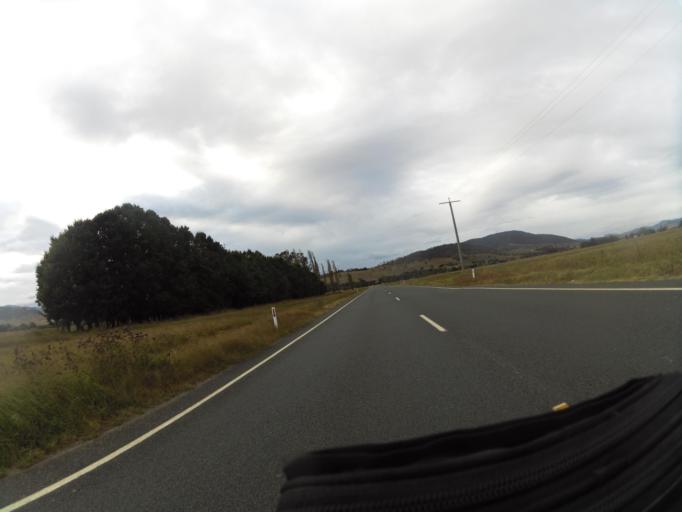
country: AU
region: New South Wales
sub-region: Snowy River
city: Jindabyne
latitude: -36.1161
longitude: 147.9795
